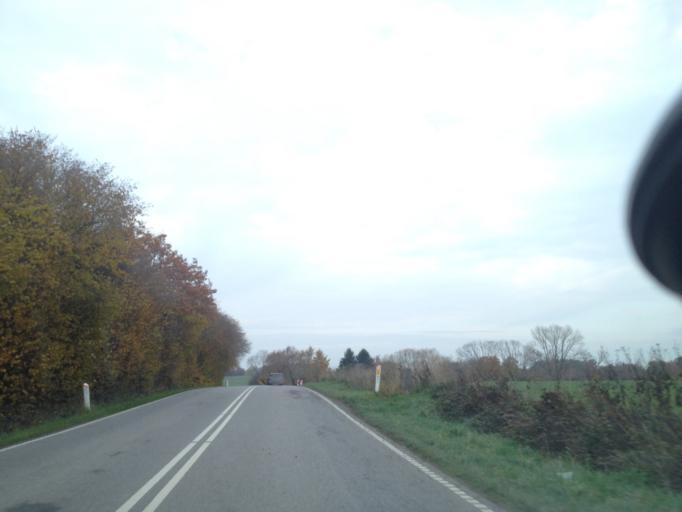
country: DK
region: South Denmark
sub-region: Assens Kommune
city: Vissenbjerg
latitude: 55.4533
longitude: 10.1210
